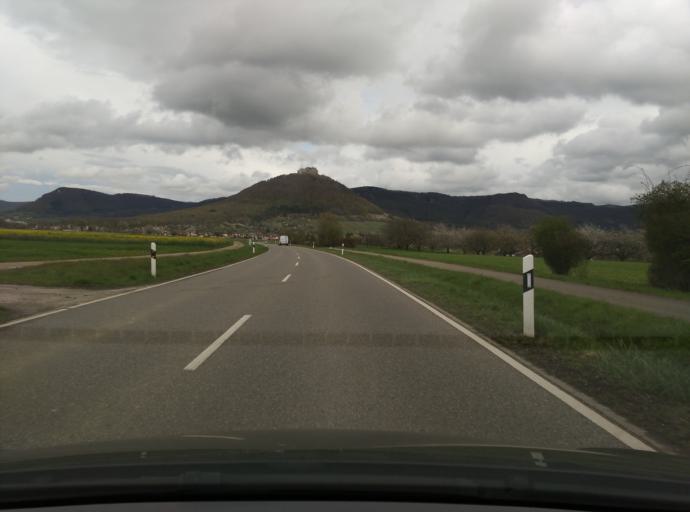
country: DE
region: Baden-Wuerttemberg
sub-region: Regierungsbezirk Stuttgart
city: Neuffen
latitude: 48.5572
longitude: 9.3569
